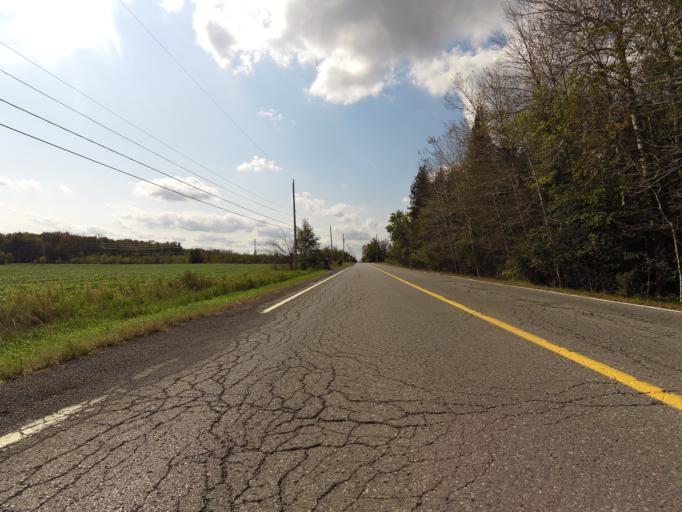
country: CA
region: Ontario
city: Bells Corners
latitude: 45.2364
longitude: -75.7239
